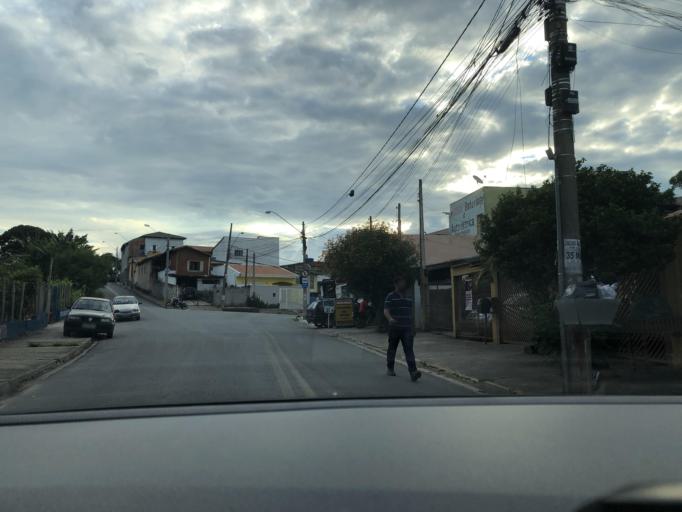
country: BR
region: Sao Paulo
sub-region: Varzea Paulista
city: Varzea Paulista
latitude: -23.2177
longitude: -46.8506
